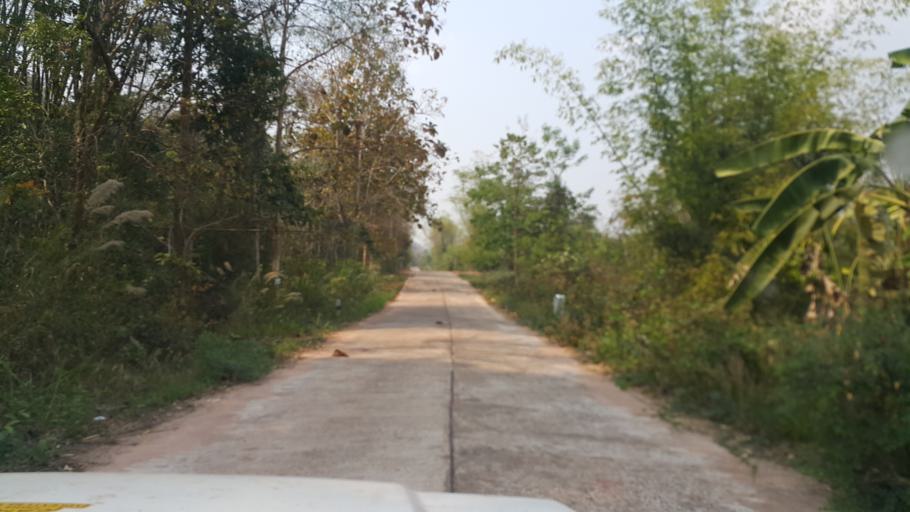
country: TH
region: Nakhon Phanom
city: Ban Phaeng
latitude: 17.9573
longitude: 104.1579
